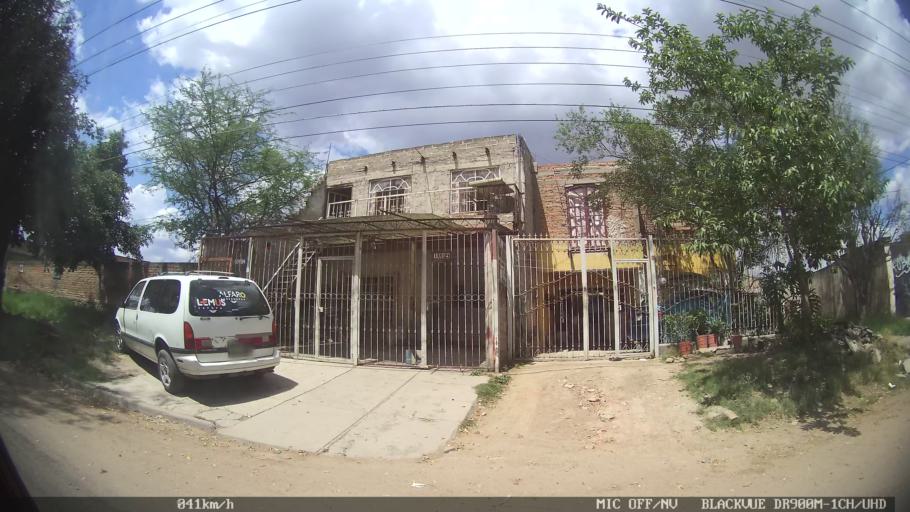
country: MX
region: Jalisco
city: Tlaquepaque
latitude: 20.6749
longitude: -103.2646
